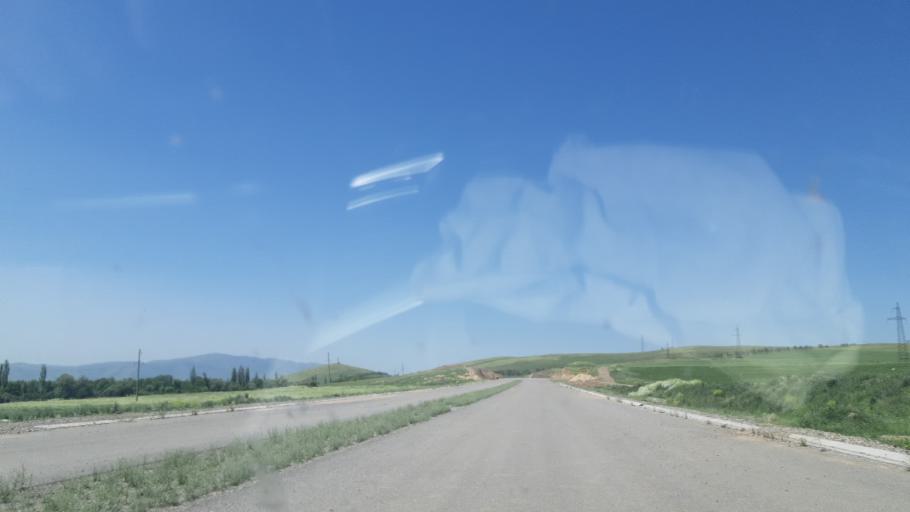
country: KZ
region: Ongtustik Qazaqstan
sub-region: Tulkibas Audany
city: Zhabagly
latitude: 42.5176
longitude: 70.5486
